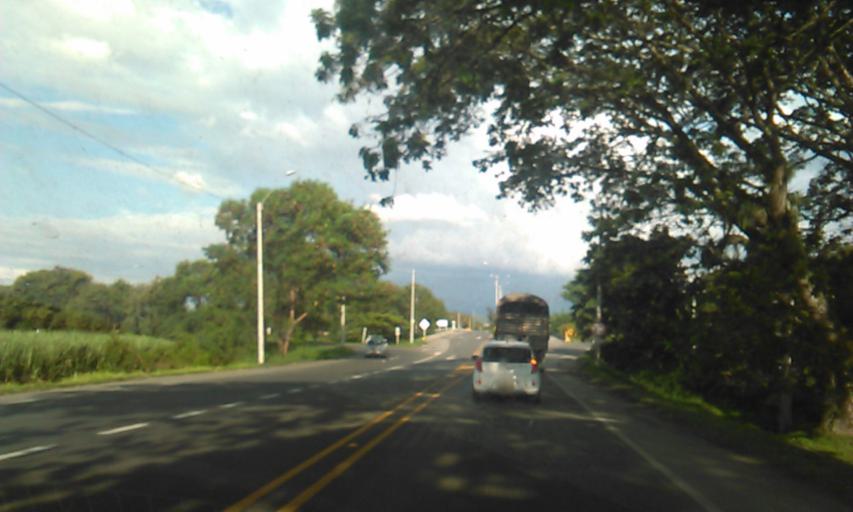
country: CO
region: Valle del Cauca
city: Buga
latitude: 3.8928
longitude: -76.3145
